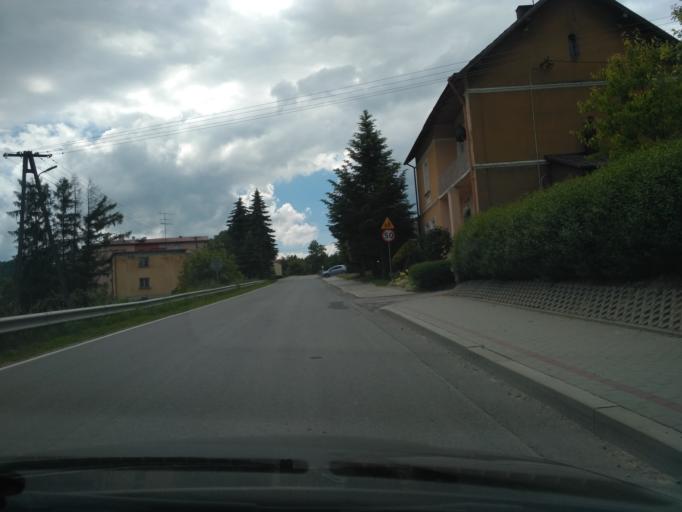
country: PL
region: Subcarpathian Voivodeship
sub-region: Powiat przeworski
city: Jawornik Polski
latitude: 49.8921
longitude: 22.2901
